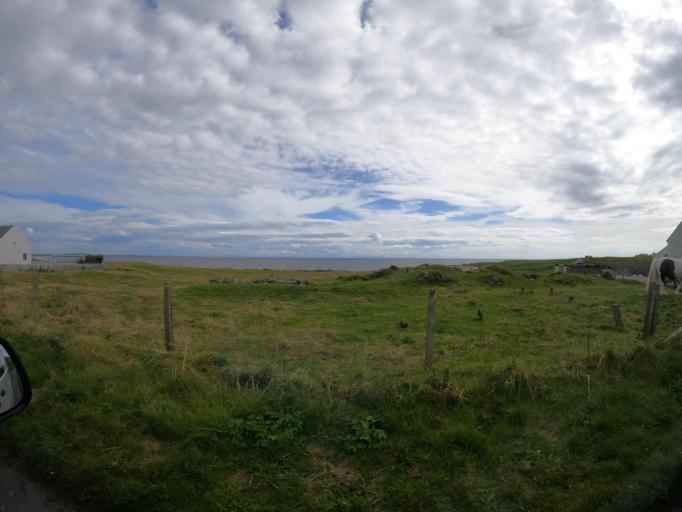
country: GB
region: Scotland
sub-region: Eilean Siar
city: Barra
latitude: 56.4712
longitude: -6.8993
